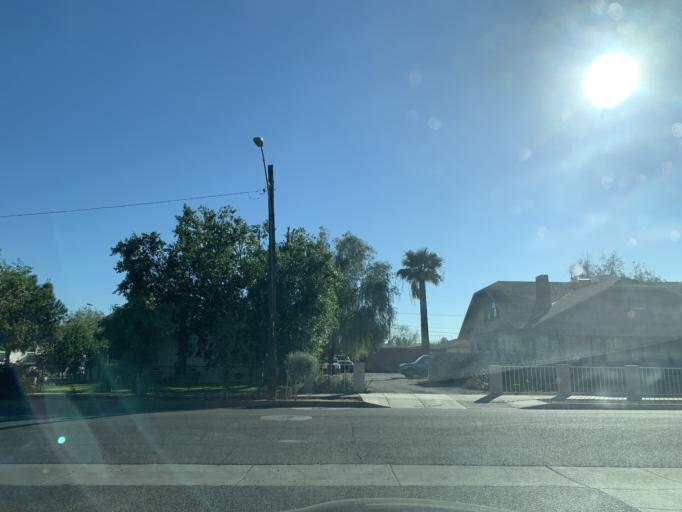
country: US
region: Arizona
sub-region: Maricopa County
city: Phoenix
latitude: 33.4598
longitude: -112.0531
